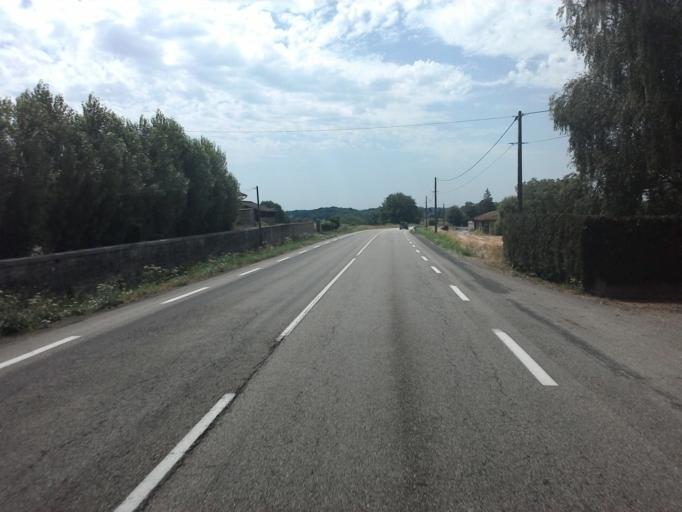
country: FR
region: Rhone-Alpes
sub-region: Departement de l'Ain
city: Coligny
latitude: 46.3372
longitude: 5.3183
